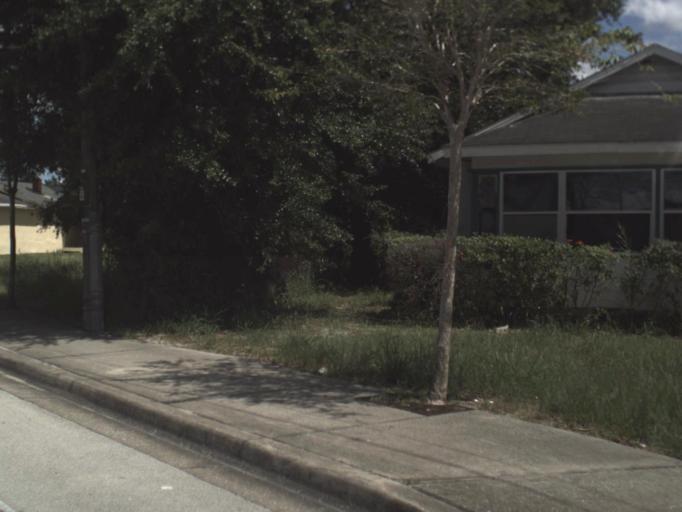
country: US
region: Florida
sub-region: Polk County
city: Winter Haven
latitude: 28.0482
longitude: -81.7238
